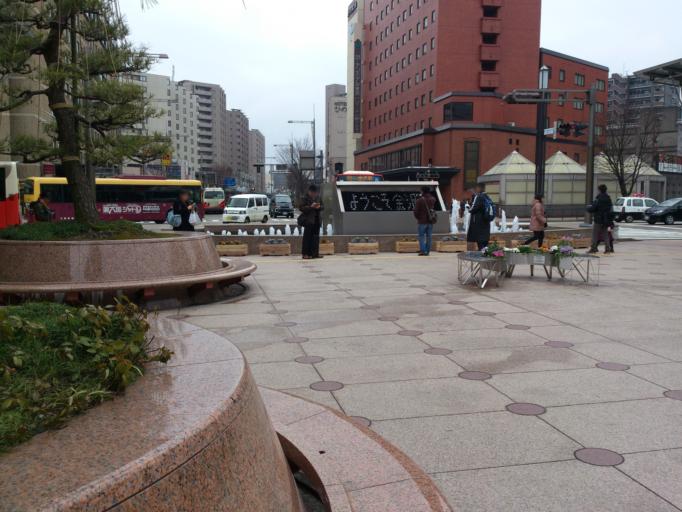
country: JP
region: Ishikawa
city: Kanazawa-shi
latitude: 36.5778
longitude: 136.6493
